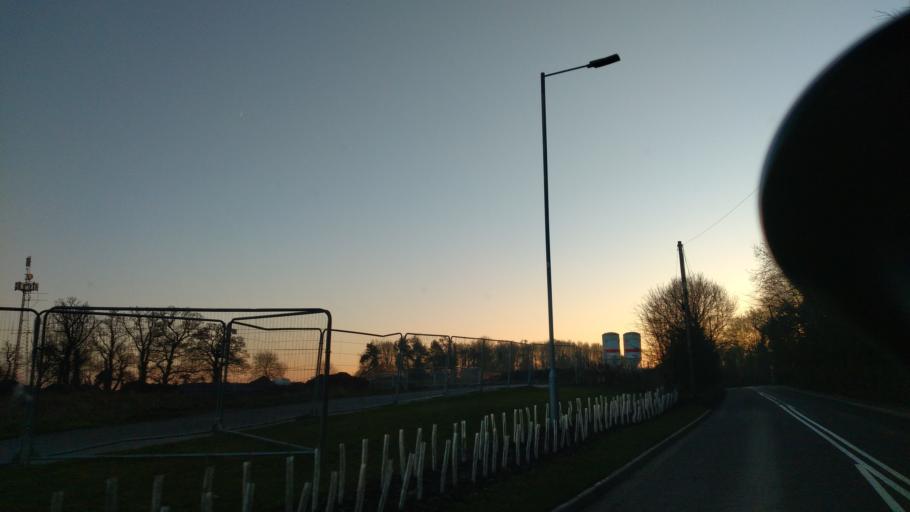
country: GB
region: England
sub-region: Wiltshire
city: Calne
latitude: 51.4305
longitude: -2.0060
